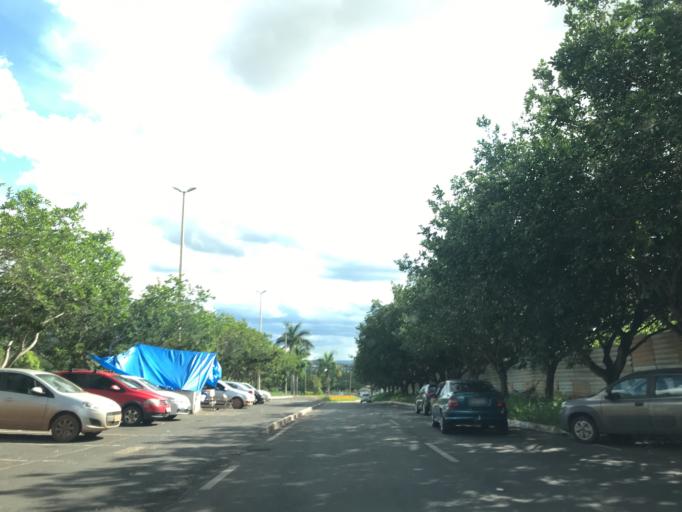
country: BR
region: Federal District
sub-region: Brasilia
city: Brasilia
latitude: -15.8080
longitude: -47.8688
